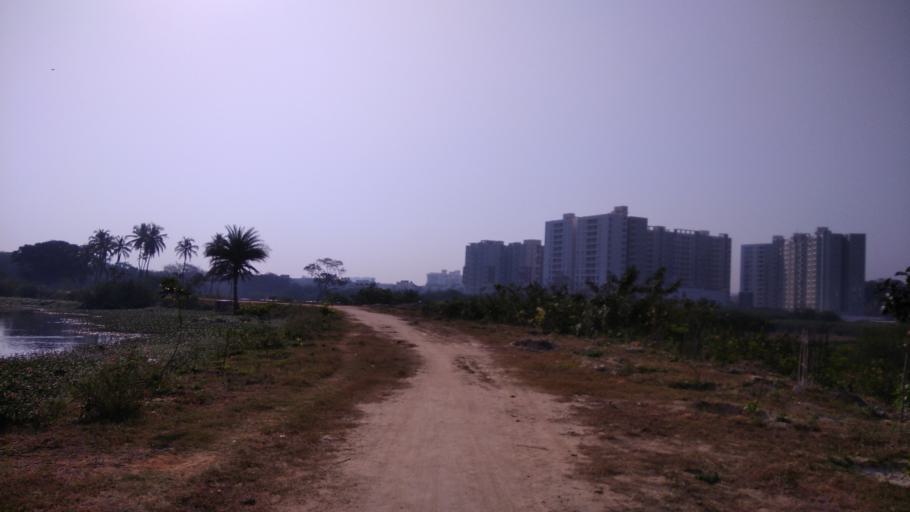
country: IN
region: Karnataka
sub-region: Bangalore Rural
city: Hoskote
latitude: 12.9737
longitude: 77.7372
